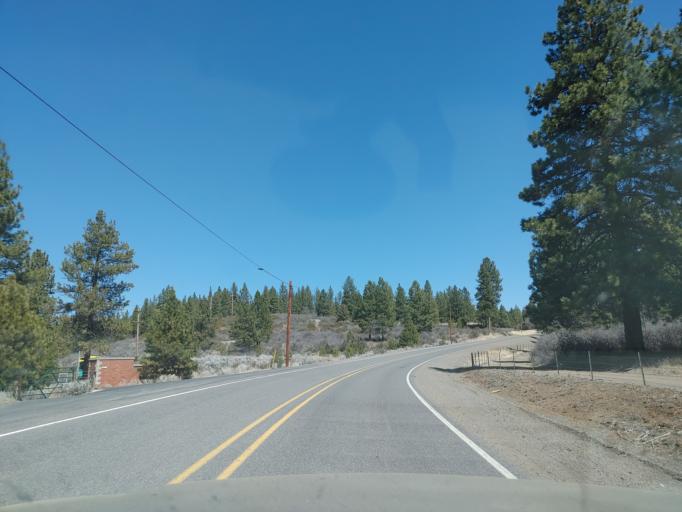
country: US
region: Oregon
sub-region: Klamath County
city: Klamath Falls
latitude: 42.5578
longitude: -121.8936
